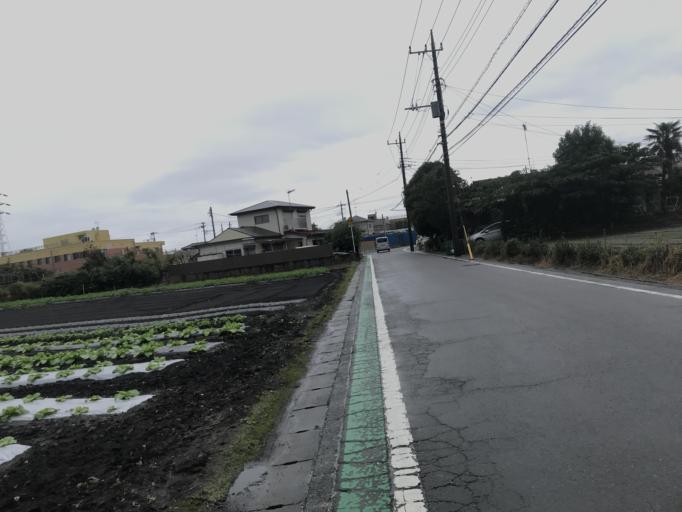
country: JP
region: Kanagawa
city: Zama
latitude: 35.5536
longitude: 139.3306
